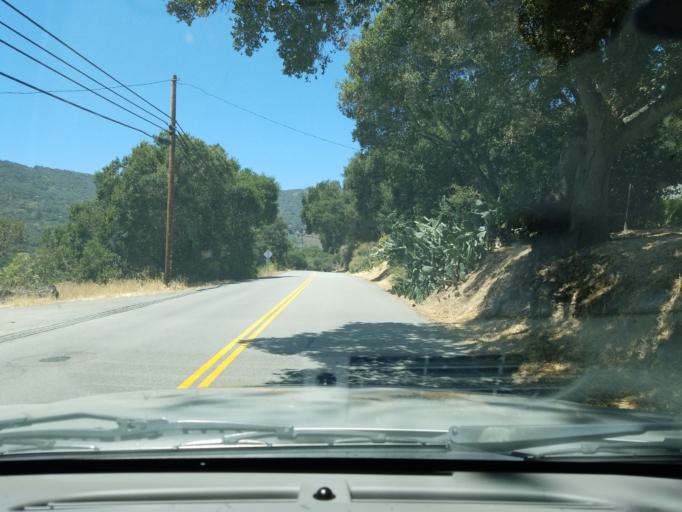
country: US
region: California
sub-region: Monterey County
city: Carmel Valley Village
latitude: 36.4761
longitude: -121.7226
